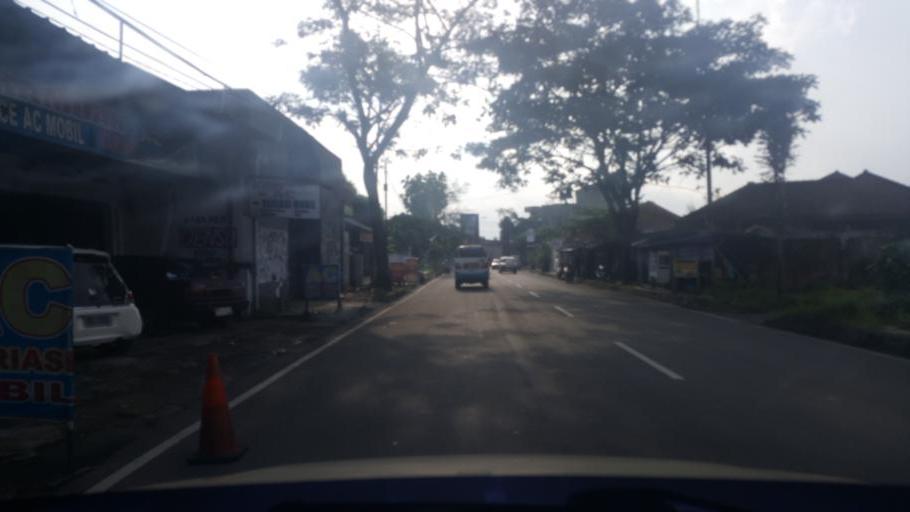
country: ID
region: West Java
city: Tawangsari
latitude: -7.3192
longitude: 108.2233
